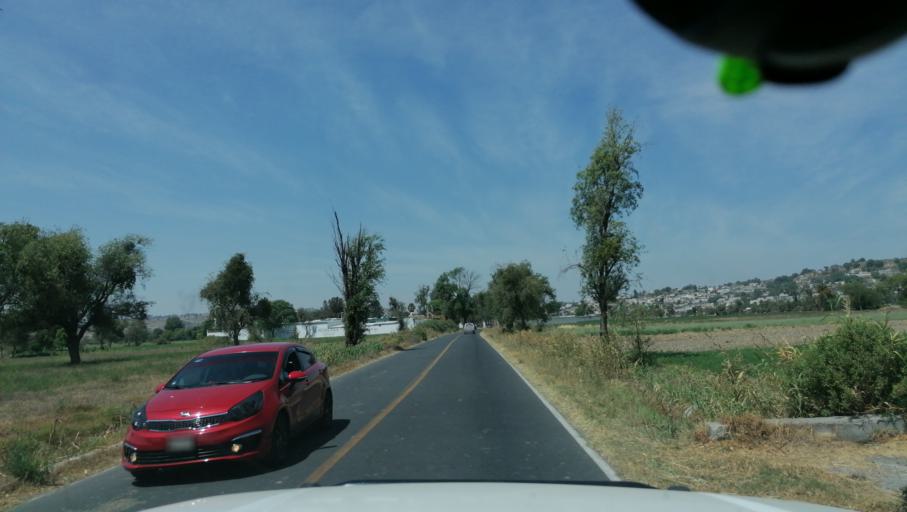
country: MX
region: Tlaxcala
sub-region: Tetlatlahuca
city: Tetlatlahuca
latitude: 19.2221
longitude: -98.2927
